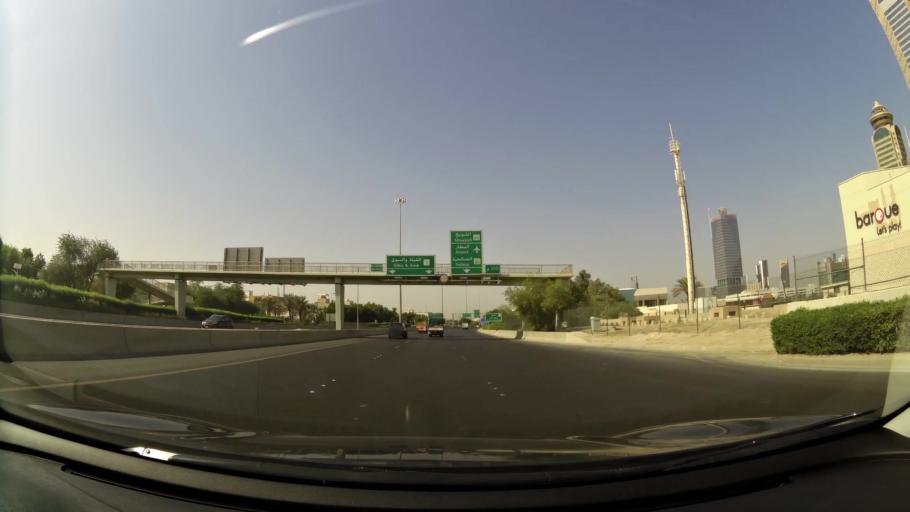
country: KW
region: Al Asimah
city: Kuwait City
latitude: 29.3595
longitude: 47.9823
